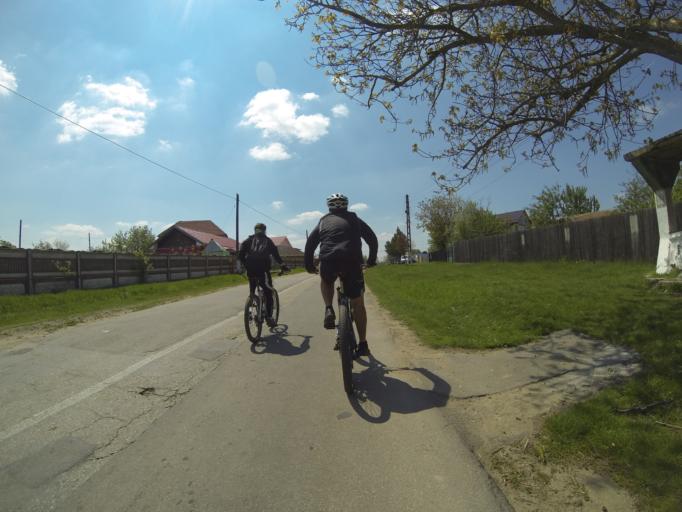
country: RO
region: Dolj
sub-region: Comuna Salcuta
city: Salcuta
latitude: 44.2522
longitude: 23.4199
